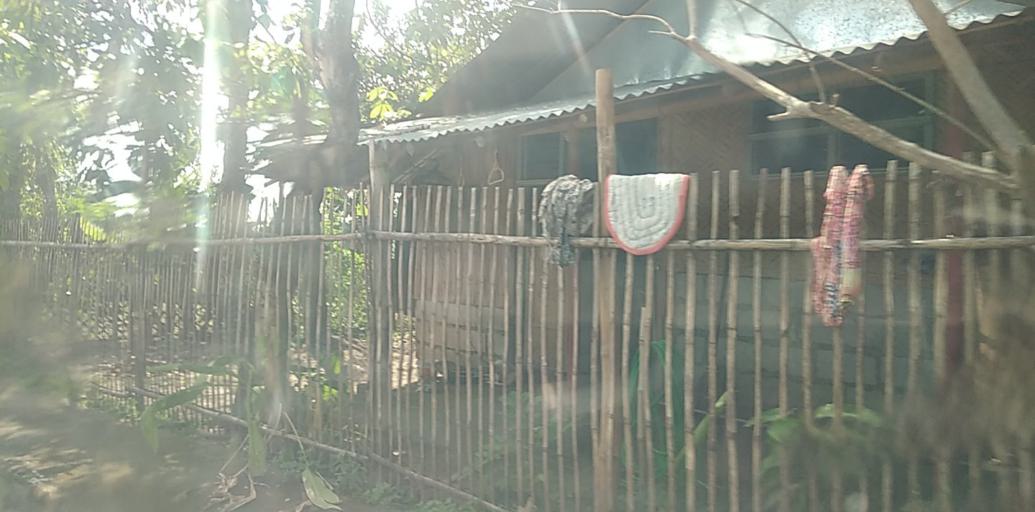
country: PH
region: Central Luzon
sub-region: Province of Pampanga
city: Buensuseso
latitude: 15.1911
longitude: 120.6606
